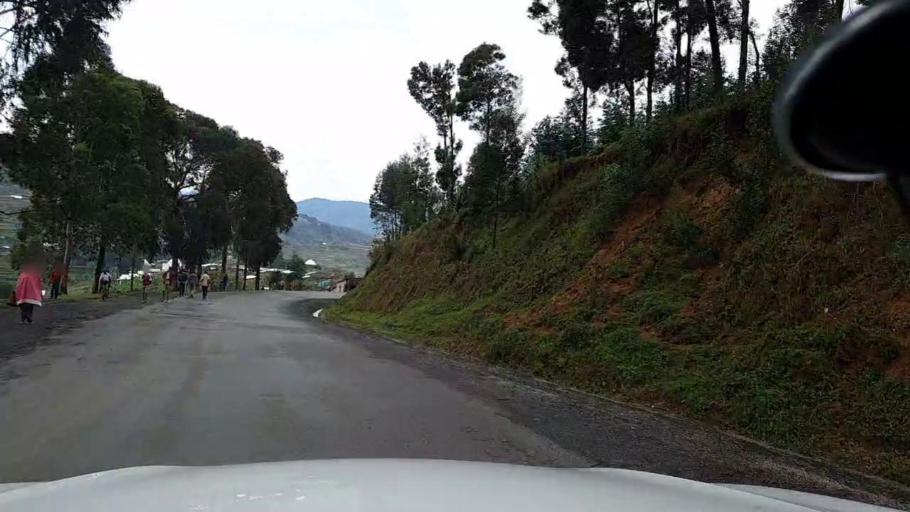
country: RW
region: Western Province
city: Kibuye
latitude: -2.0661
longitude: 29.5401
